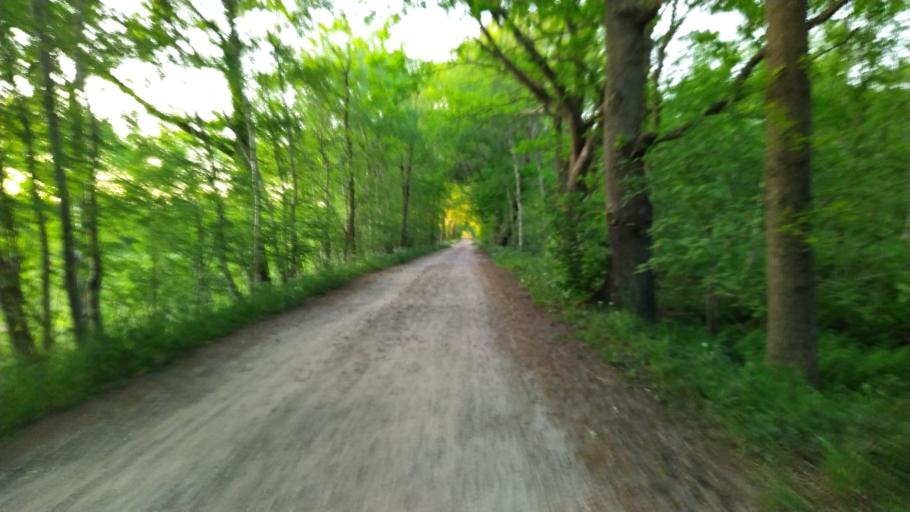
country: DE
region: Lower Saxony
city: Bargstedt
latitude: 53.4845
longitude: 9.4401
